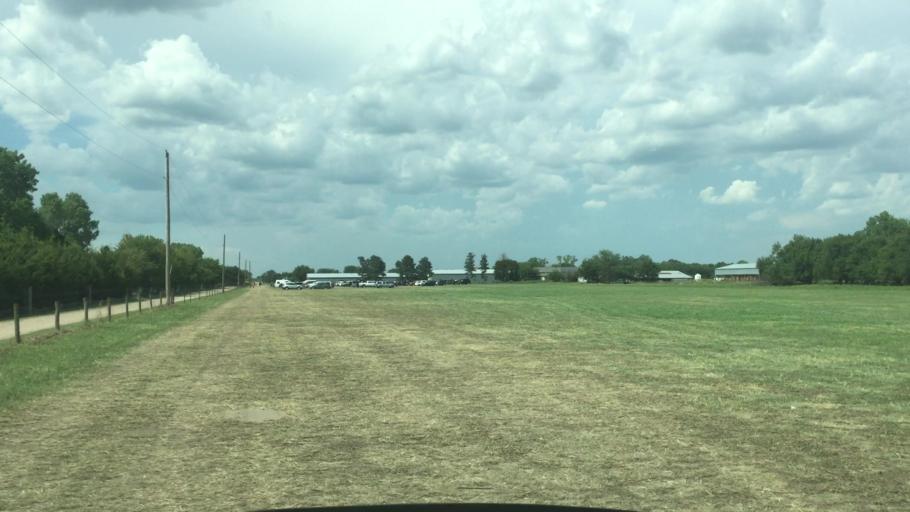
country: US
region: Kansas
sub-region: Sedgwick County
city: Maize
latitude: 37.7816
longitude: -97.4356
